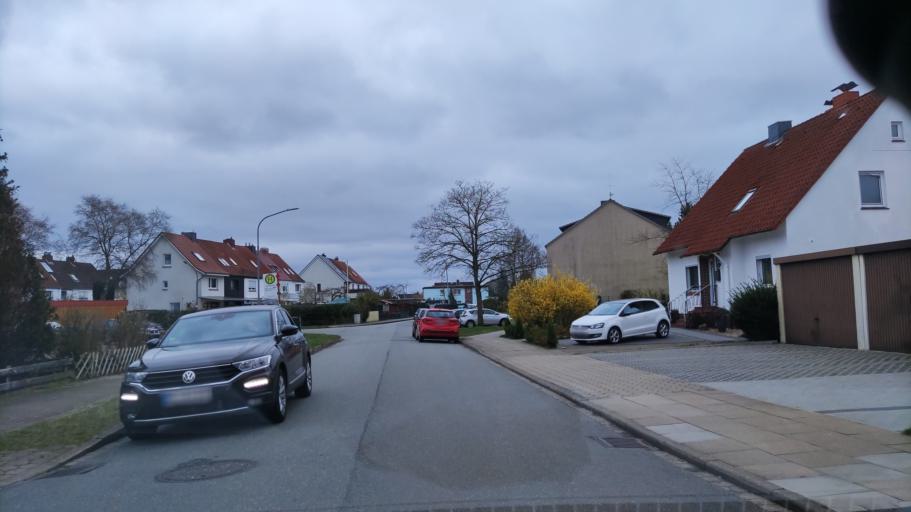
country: DE
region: Lower Saxony
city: Winsen
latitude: 53.3605
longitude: 10.2179
